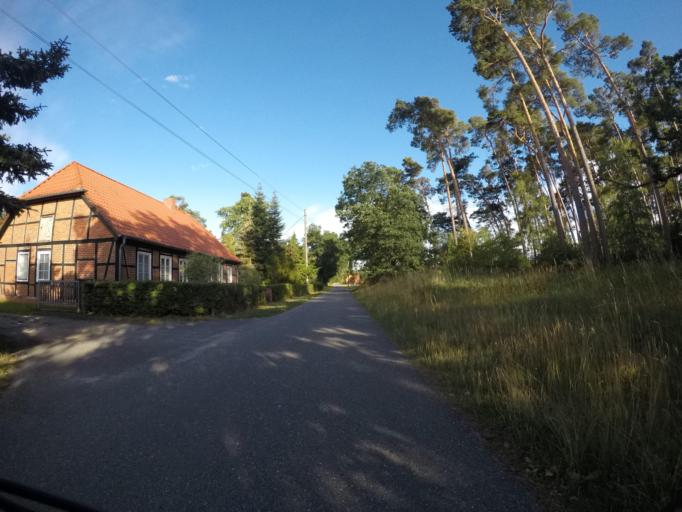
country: DE
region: Mecklenburg-Vorpommern
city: Lubtheen
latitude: 53.2349
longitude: 11.0416
